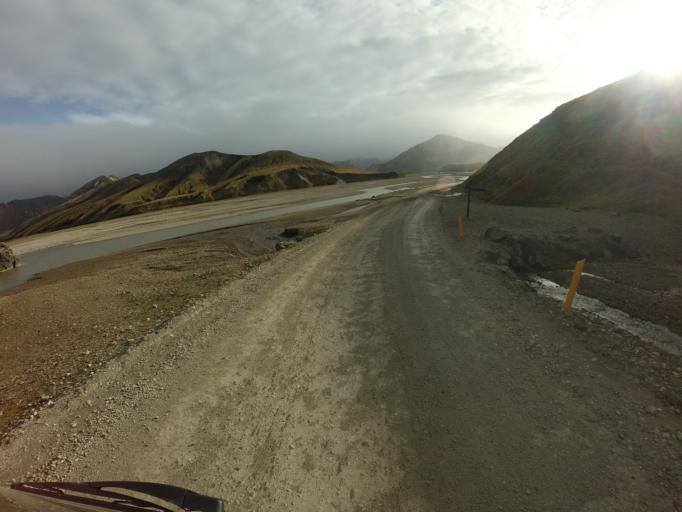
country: IS
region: South
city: Vestmannaeyjar
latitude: 63.9987
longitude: -19.0509
